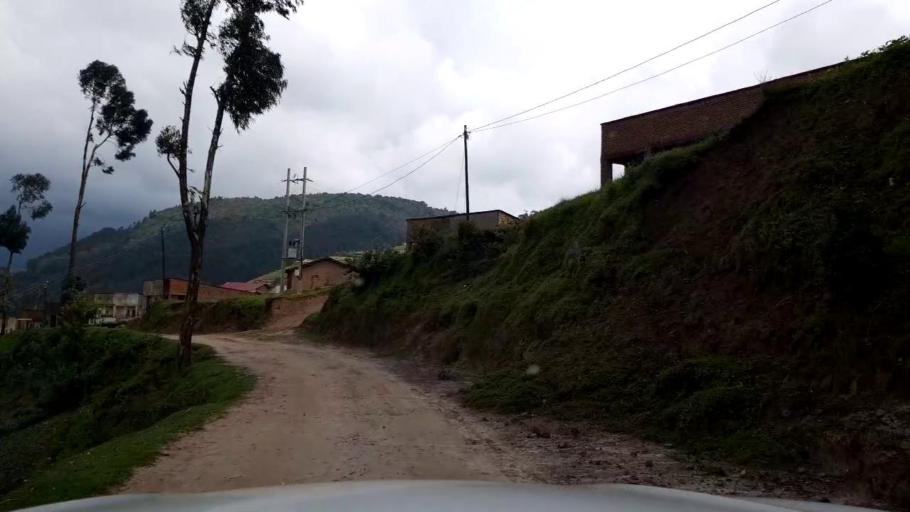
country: RW
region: Western Province
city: Kibuye
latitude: -1.9633
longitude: 29.4808
